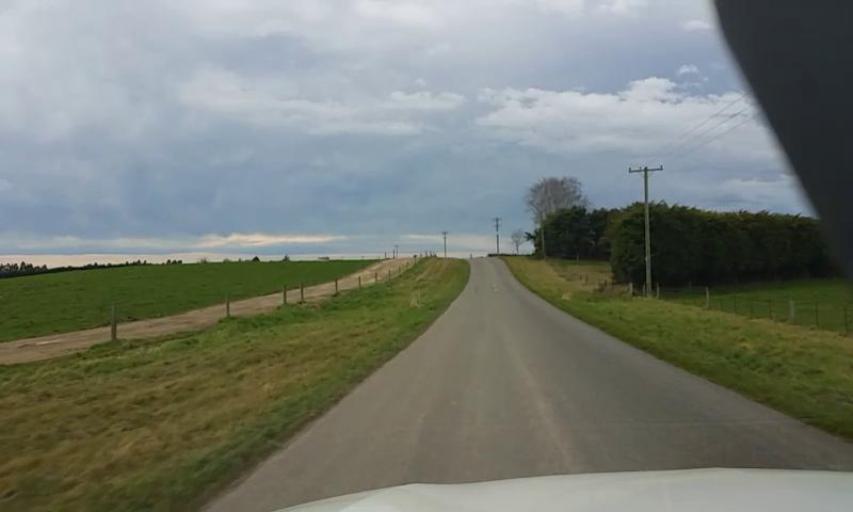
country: NZ
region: Canterbury
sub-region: Waimakariri District
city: Kaiapoi
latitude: -43.2958
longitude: 172.4754
